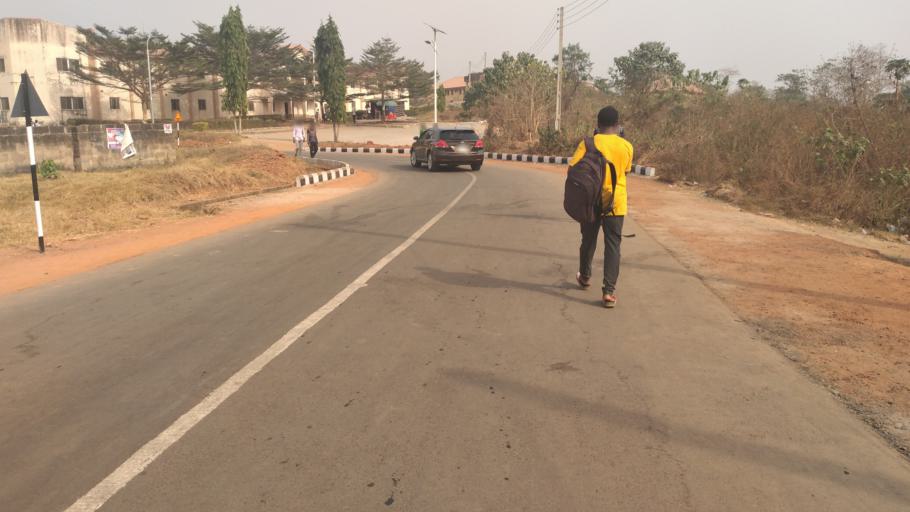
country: NG
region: Ondo
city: Ilare
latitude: 7.3021
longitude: 5.1422
